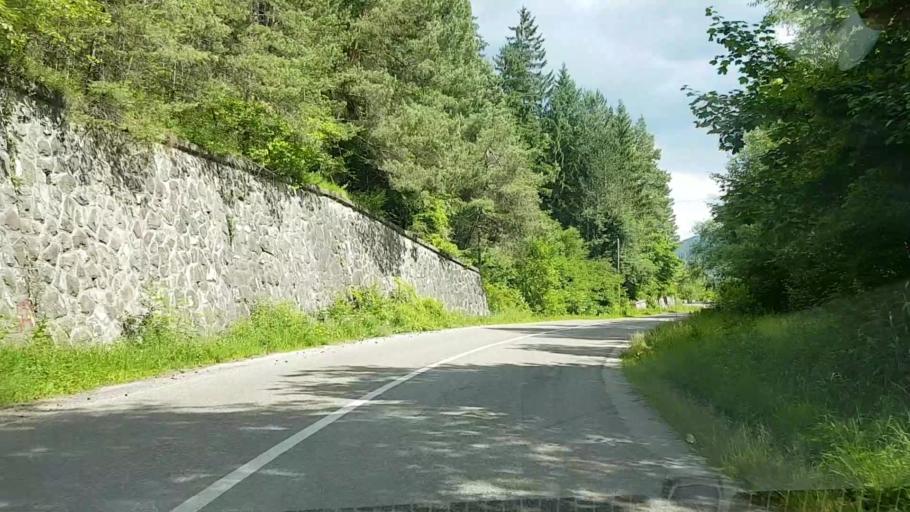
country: RO
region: Neamt
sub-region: Comuna Ceahlau
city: Ceahlau
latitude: 47.0541
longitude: 25.9783
